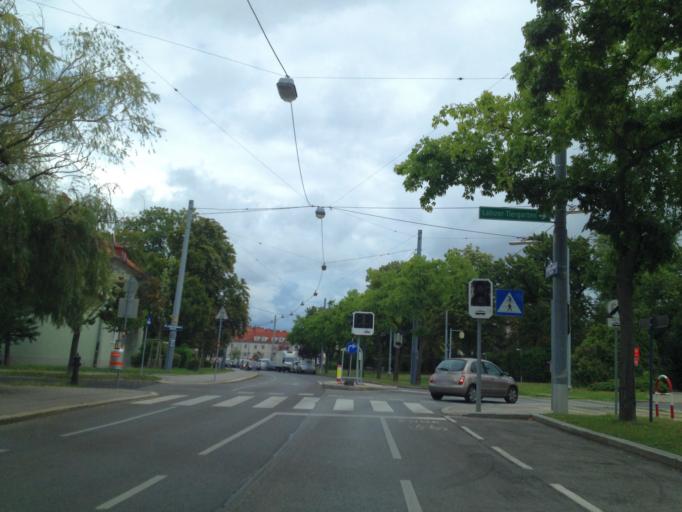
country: AT
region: Lower Austria
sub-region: Politischer Bezirk Modling
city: Perchtoldsdorf
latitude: 48.1684
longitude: 16.2809
